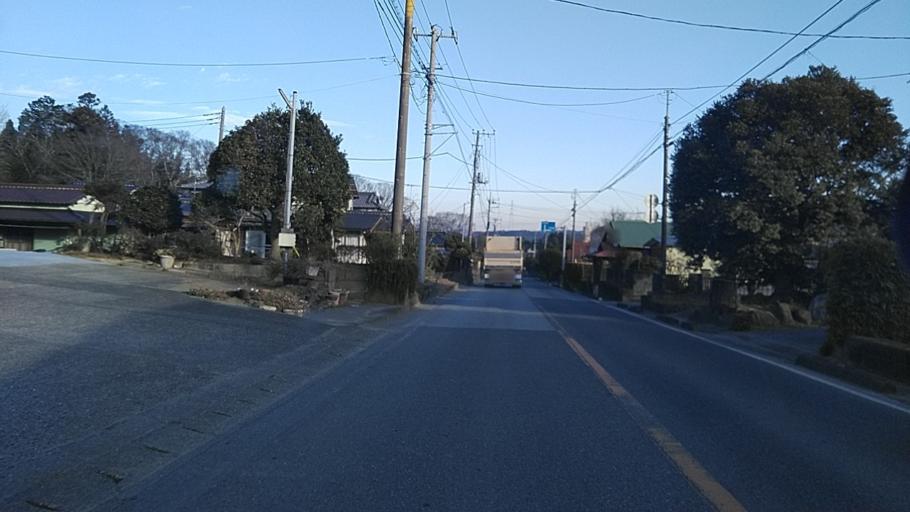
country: JP
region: Chiba
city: Kimitsu
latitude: 35.2673
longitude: 139.9912
